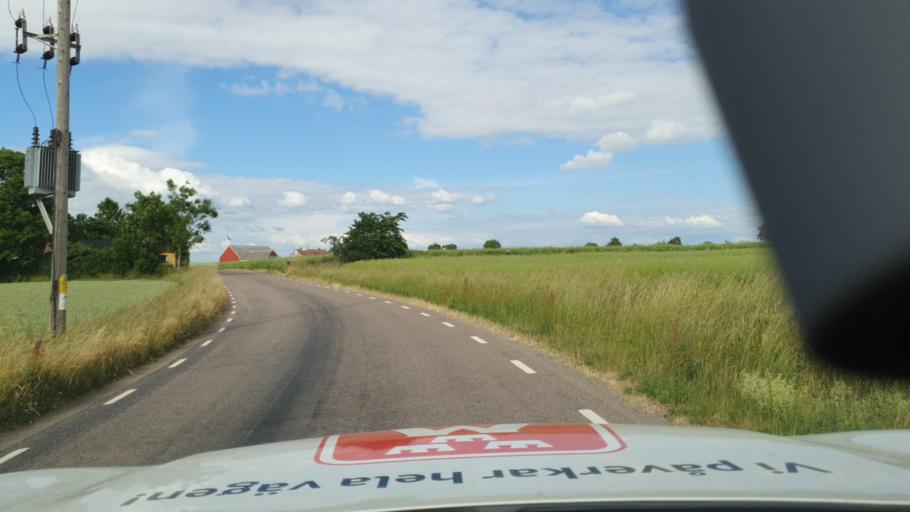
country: SE
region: Skane
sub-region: Skurups Kommun
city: Skurup
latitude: 55.4411
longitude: 13.4540
